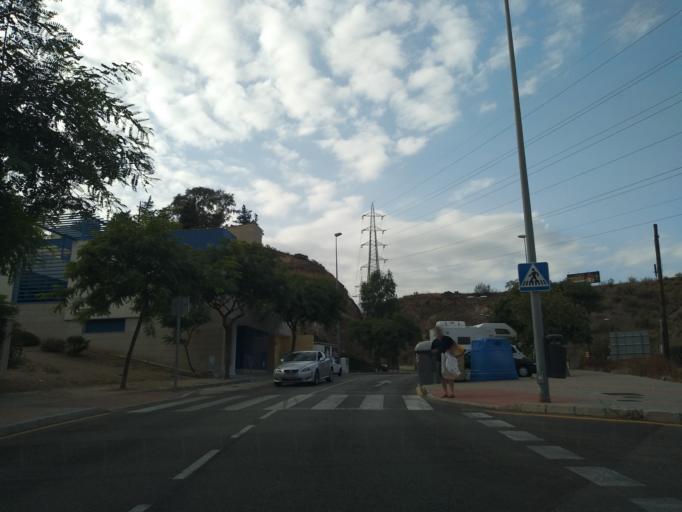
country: ES
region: Andalusia
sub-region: Provincia de Malaga
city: Malaga
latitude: 36.7322
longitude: -4.4756
